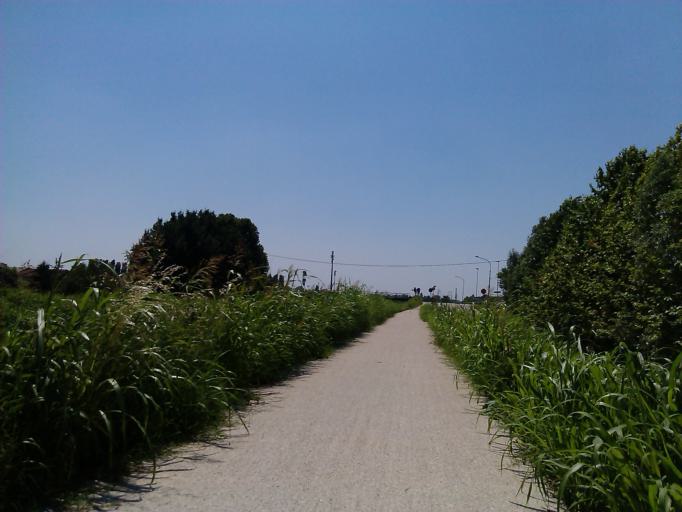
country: IT
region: Veneto
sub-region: Provincia di Padova
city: Loreggia
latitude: 45.5949
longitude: 11.9360
